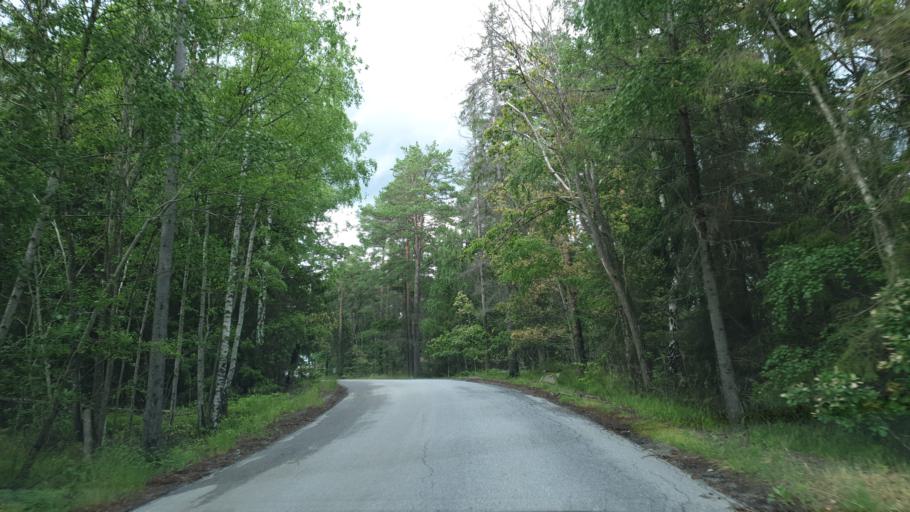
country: SE
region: Stockholm
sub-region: Jarfalla Kommun
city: Jakobsberg
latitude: 59.4265
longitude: 17.8032
